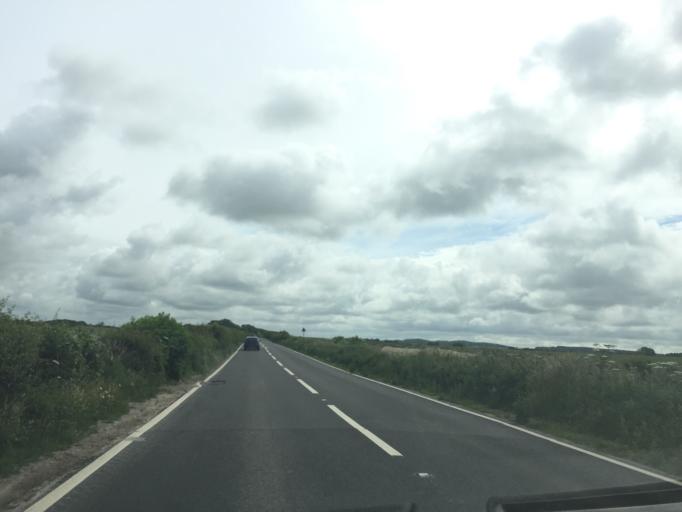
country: GB
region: England
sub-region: Dorset
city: Bovington Camp
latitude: 50.7695
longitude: -2.1791
